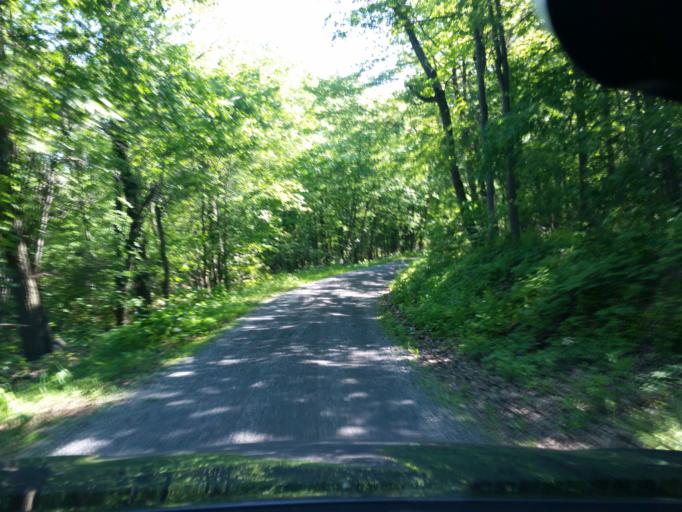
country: US
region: Pennsylvania
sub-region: Lycoming County
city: Duboistown
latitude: 41.1285
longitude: -77.0982
